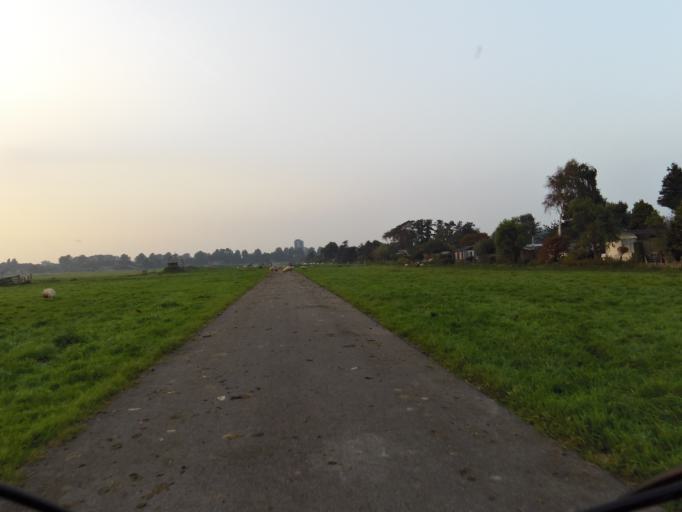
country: NL
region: South Holland
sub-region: Gemeente Leiden
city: Leiden
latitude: 52.1295
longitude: 4.4809
